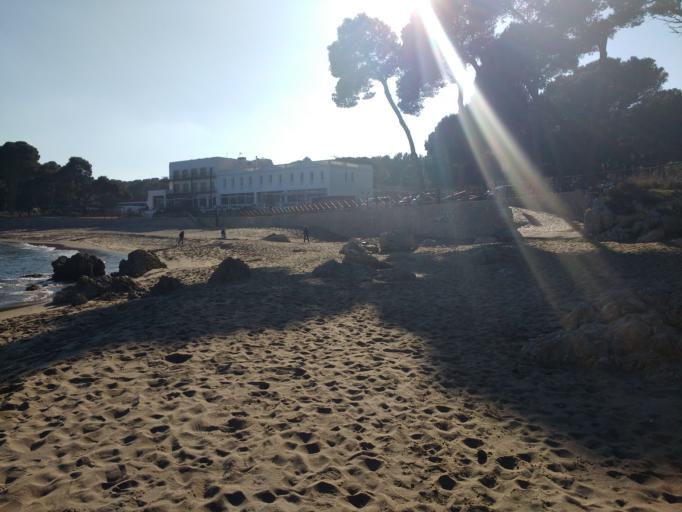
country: ES
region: Catalonia
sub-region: Provincia de Girona
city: l'Escala
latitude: 42.1325
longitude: 3.1225
